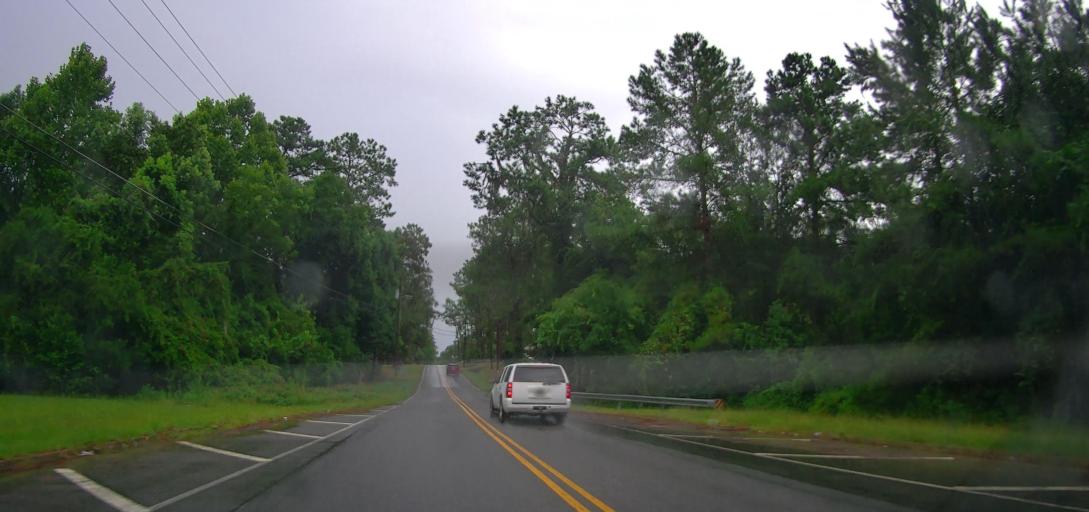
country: US
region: Georgia
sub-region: Ware County
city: Sunnyside
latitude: 31.2281
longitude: -82.3307
